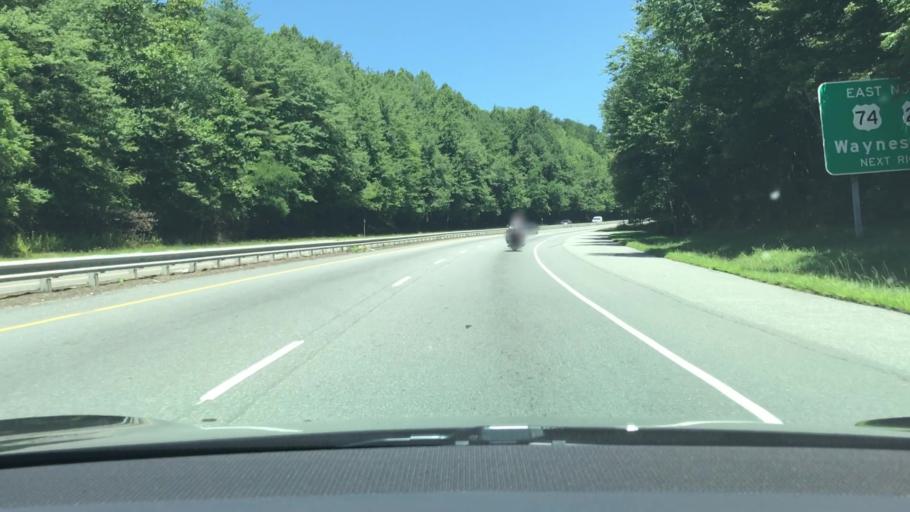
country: US
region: North Carolina
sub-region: Jackson County
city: Sylva
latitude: 35.3722
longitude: -83.2550
